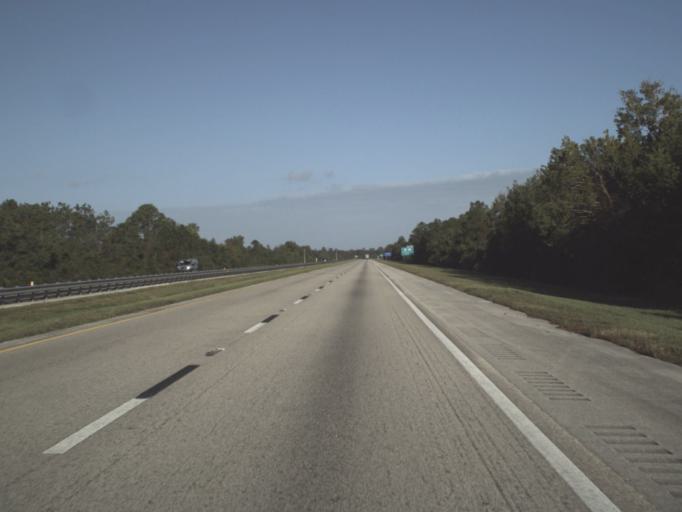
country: US
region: Florida
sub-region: Indian River County
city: Fellsmere
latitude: 27.6714
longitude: -80.8808
